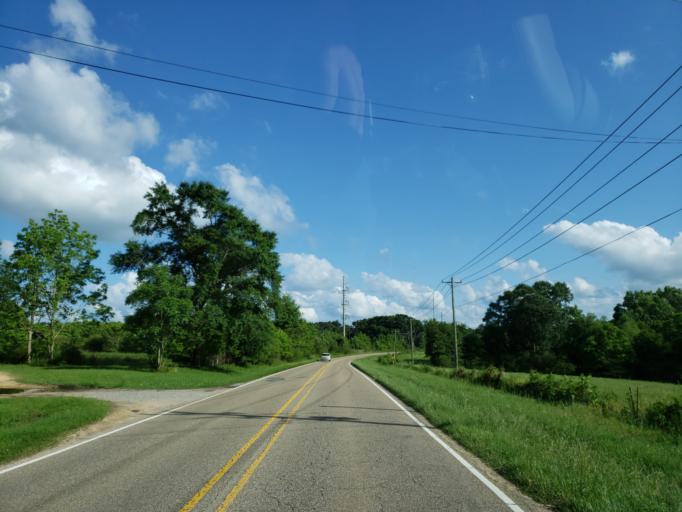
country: US
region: Mississippi
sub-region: Lamar County
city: West Hattiesburg
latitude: 31.2789
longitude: -89.4152
